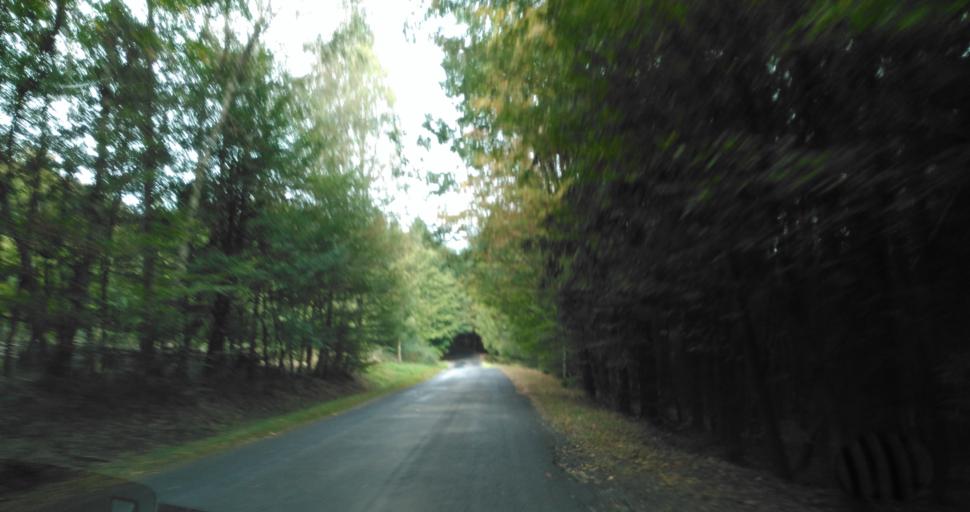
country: CZ
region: Plzensky
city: Zbiroh
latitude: 49.9389
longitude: 13.7772
